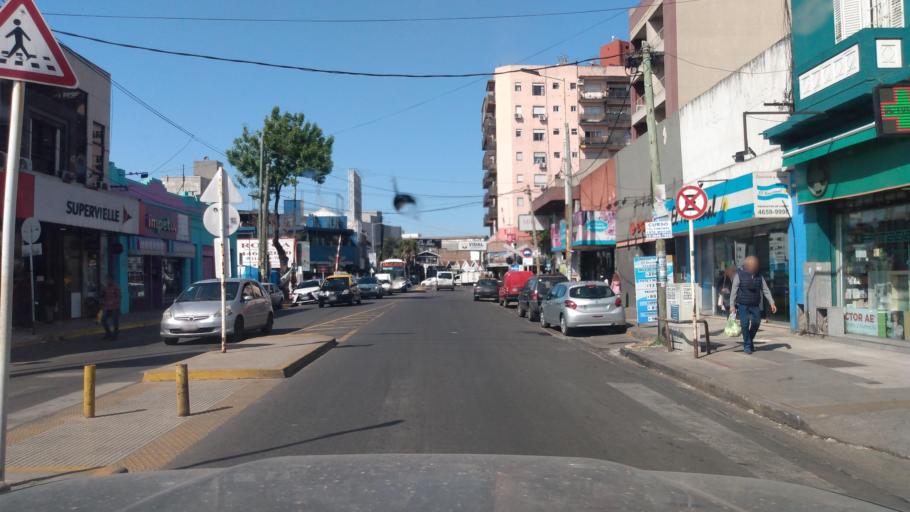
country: AR
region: Buenos Aires
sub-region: Partido de Moron
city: Moron
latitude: -34.6448
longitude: -58.5904
